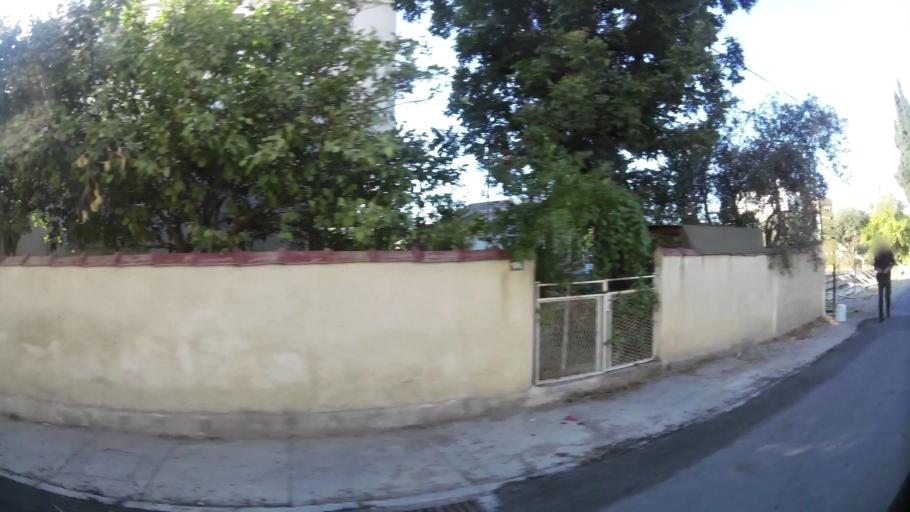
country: CY
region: Lefkosia
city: Nicosia
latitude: 35.2024
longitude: 33.3450
